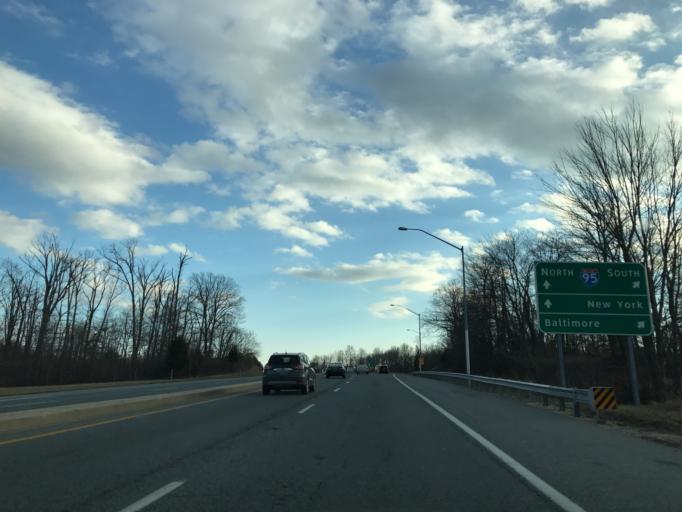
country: US
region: Maryland
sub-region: Cecil County
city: North East
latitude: 39.6365
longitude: -75.9581
